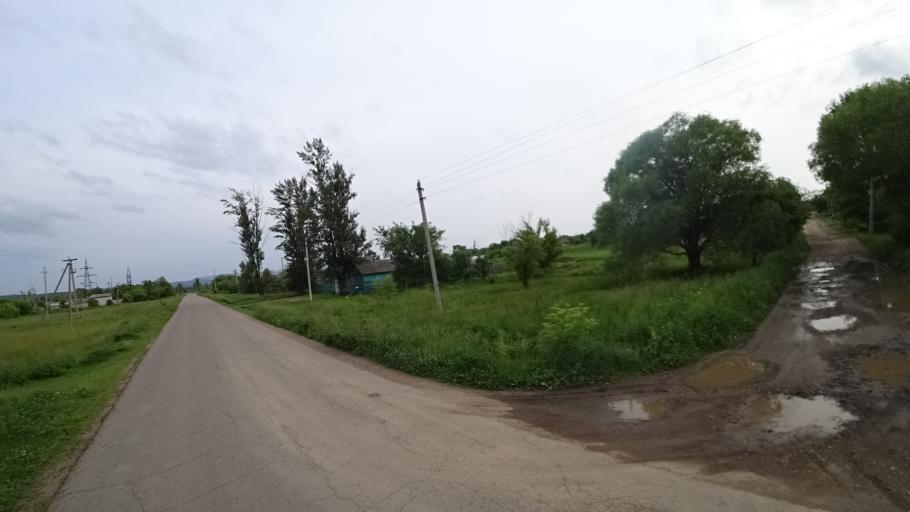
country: RU
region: Primorskiy
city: Novosysoyevka
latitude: 44.2358
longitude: 133.3699
